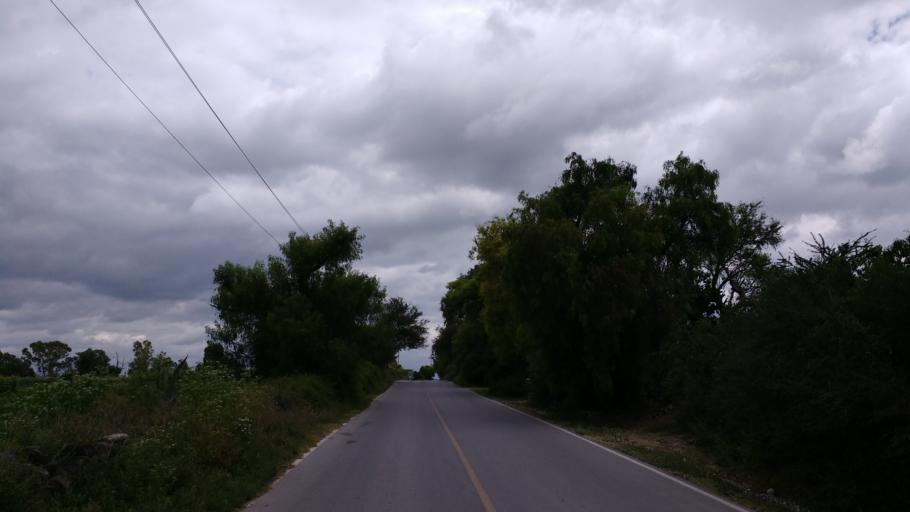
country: MX
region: Hidalgo
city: Mixquiahuala de Juarez
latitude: 20.2445
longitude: -99.2447
